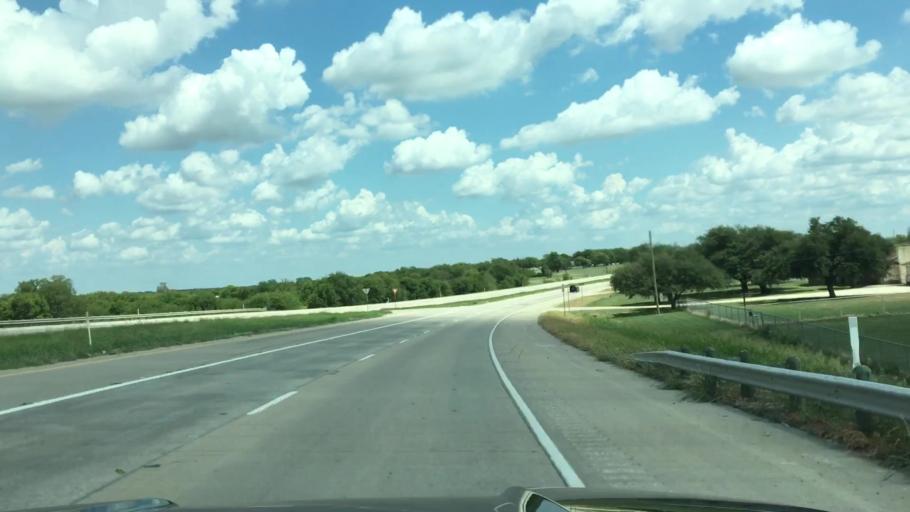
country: US
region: Texas
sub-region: Wise County
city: Rhome
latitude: 33.0461
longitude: -97.4583
